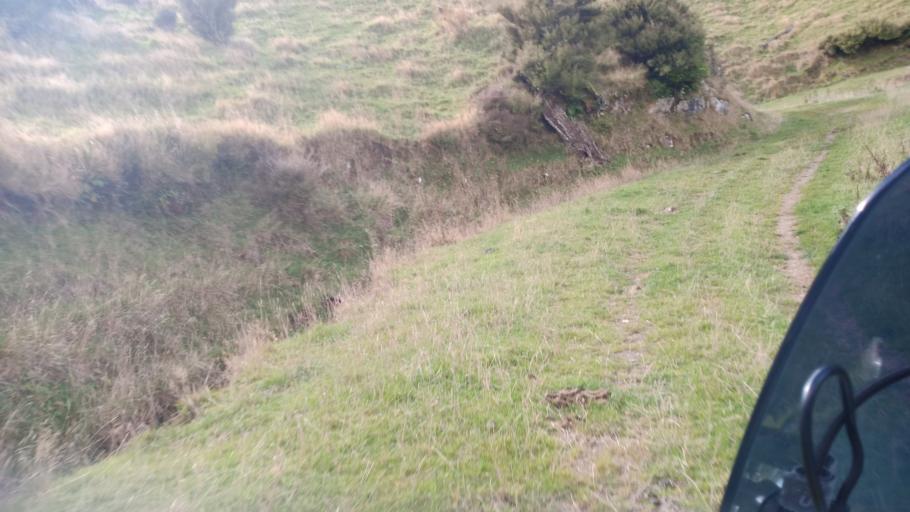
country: NZ
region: Gisborne
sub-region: Gisborne District
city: Gisborne
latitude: -38.4700
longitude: 177.5346
